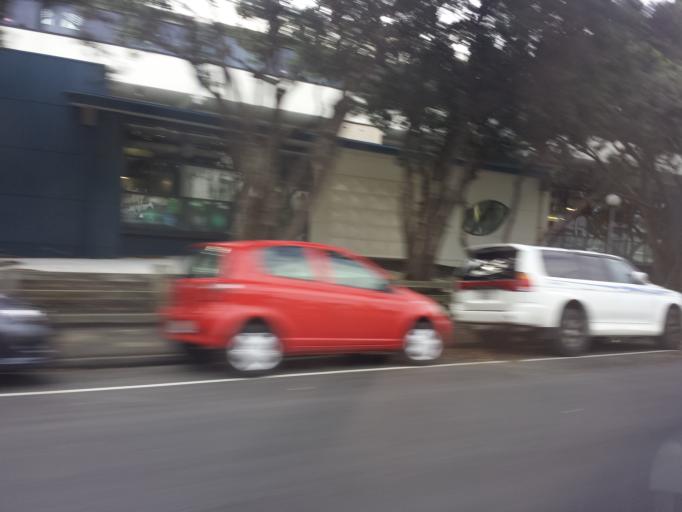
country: NZ
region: Wellington
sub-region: Wellington City
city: Wellington
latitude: -41.3155
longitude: 174.7934
